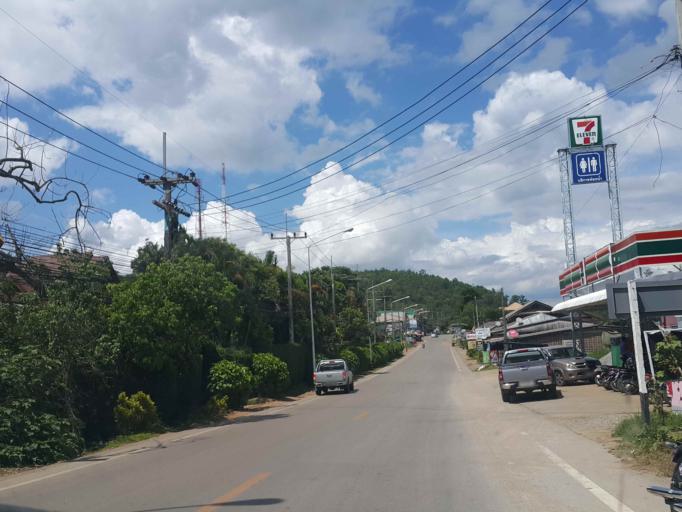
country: TH
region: Chiang Mai
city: Samoeng
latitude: 18.8920
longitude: 98.8334
